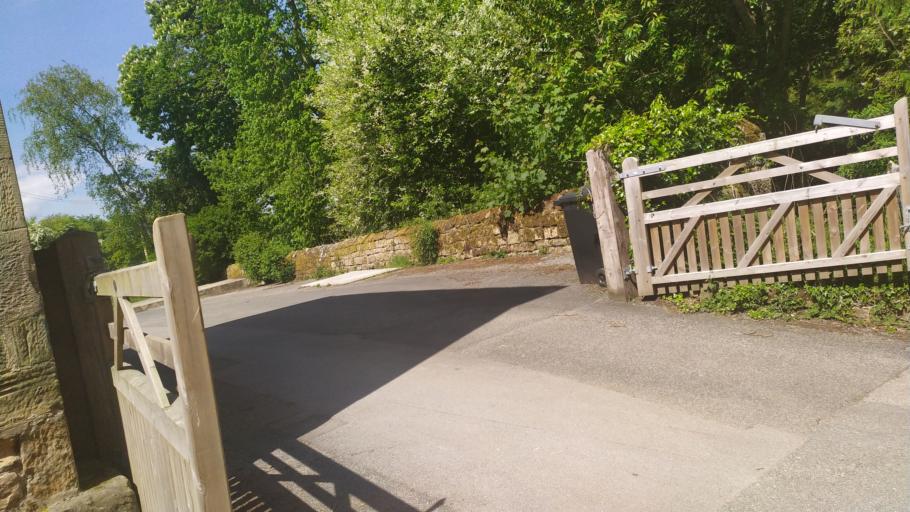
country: GB
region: England
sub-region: North Yorkshire
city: Pannal
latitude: 53.8957
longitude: -1.5357
